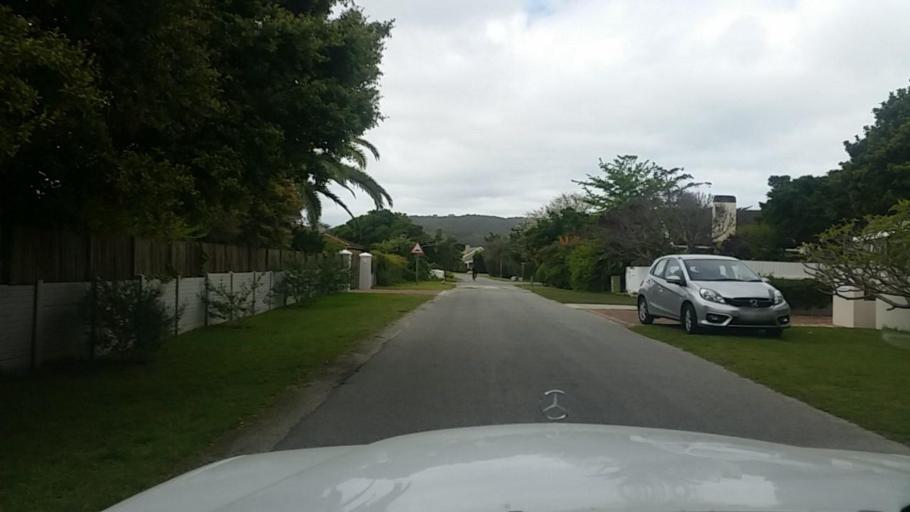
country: ZA
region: Western Cape
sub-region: Eden District Municipality
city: Knysna
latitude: -34.0680
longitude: 23.0596
